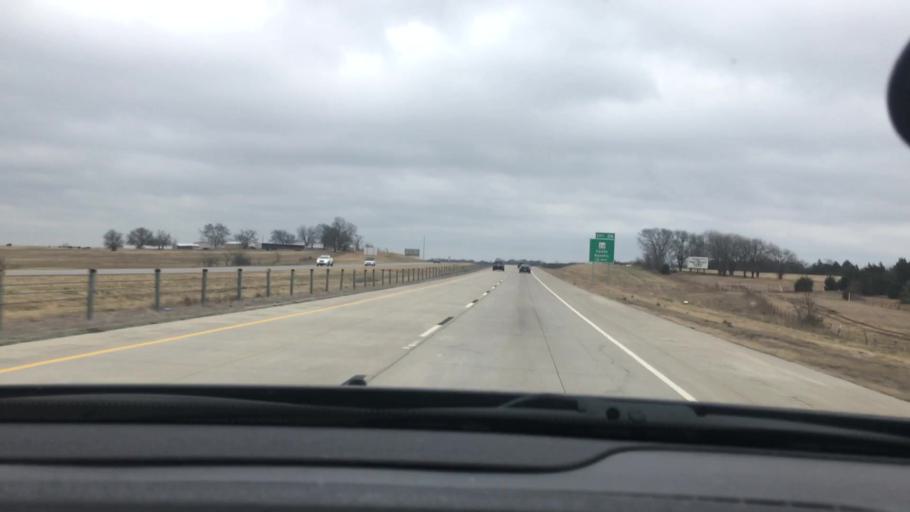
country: US
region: Oklahoma
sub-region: Bryan County
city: Durant
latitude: 34.1218
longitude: -96.2869
